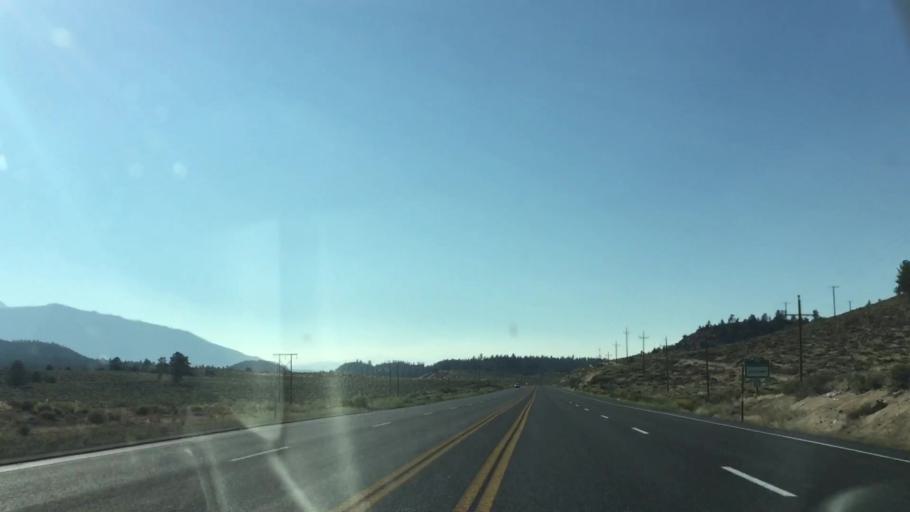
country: US
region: California
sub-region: Inyo County
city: West Bishop
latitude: 37.5525
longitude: -118.6430
